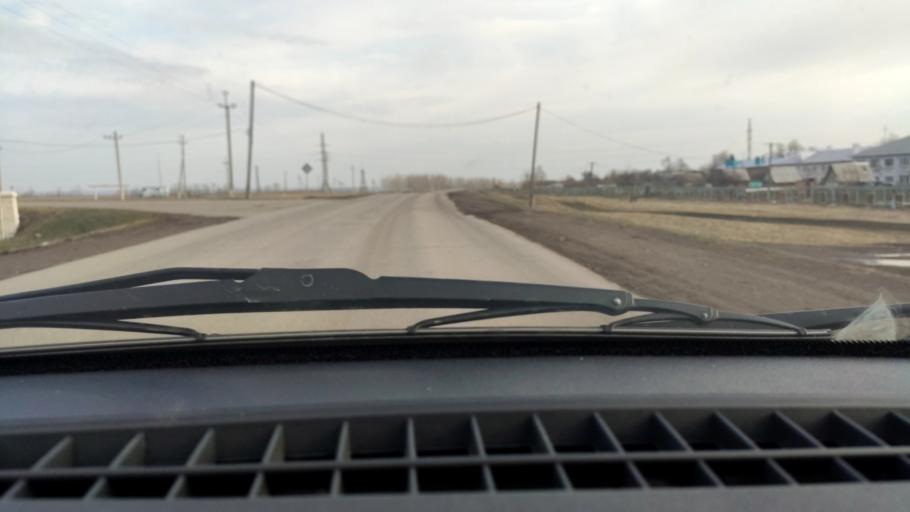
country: RU
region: Bashkortostan
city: Davlekanovo
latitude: 54.3807
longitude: 55.1958
